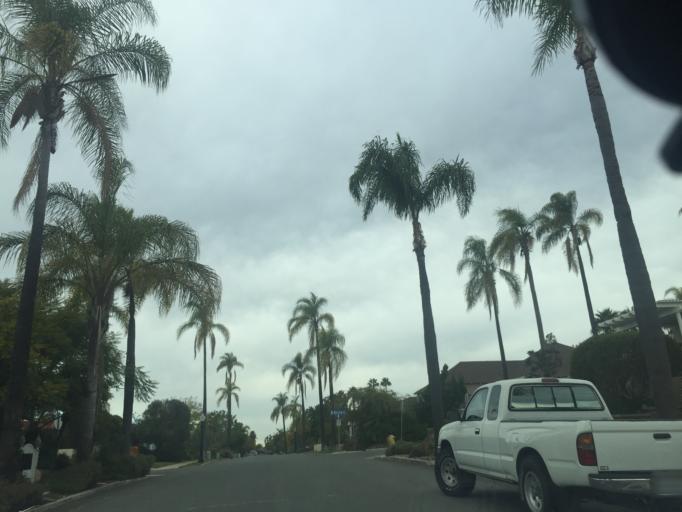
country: US
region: California
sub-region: San Diego County
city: Lemon Grove
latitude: 32.7606
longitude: -117.0935
